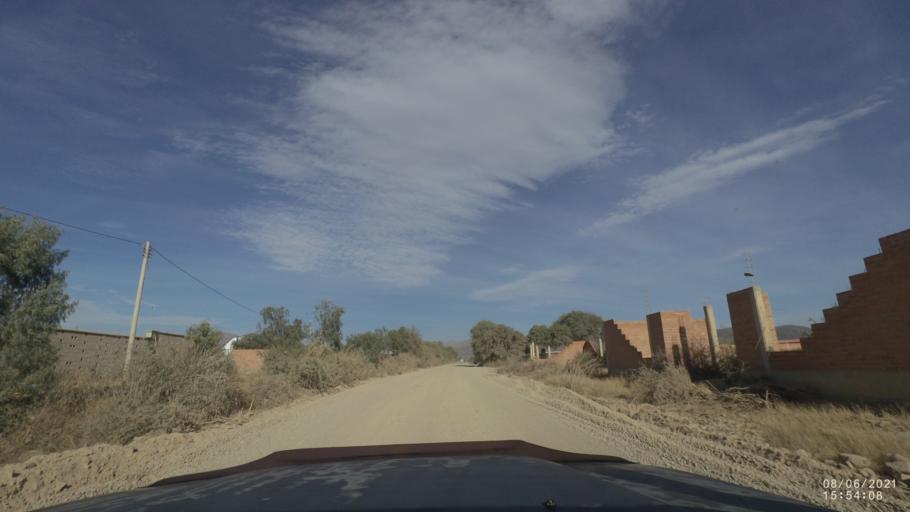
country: BO
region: Cochabamba
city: Capinota
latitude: -17.5560
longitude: -66.2548
